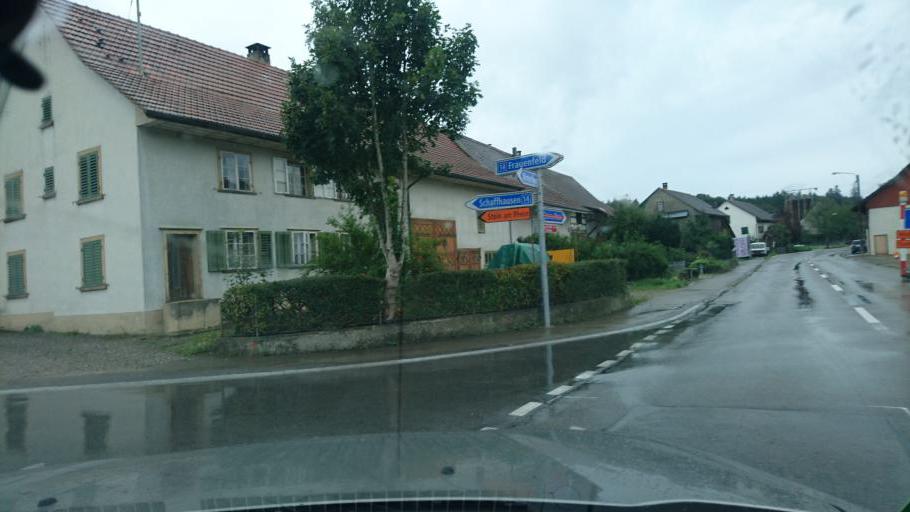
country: CH
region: Zurich
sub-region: Bezirk Andelfingen
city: Kleinandelfingen
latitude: 47.6229
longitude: 8.7402
